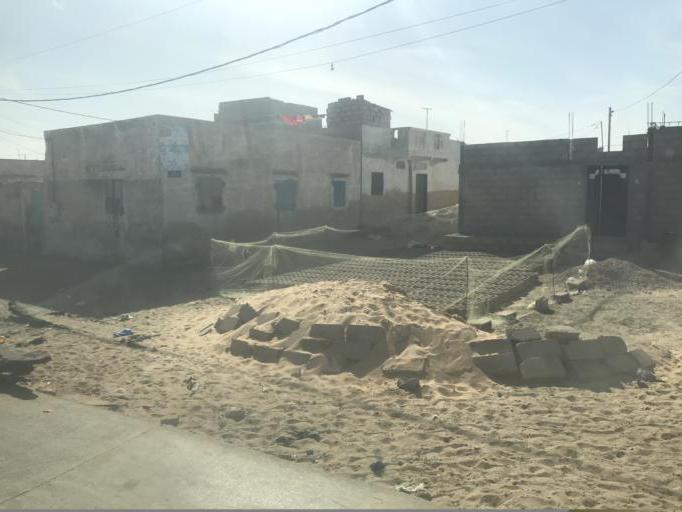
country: SN
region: Saint-Louis
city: Saint-Louis
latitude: 16.0452
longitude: -16.5055
